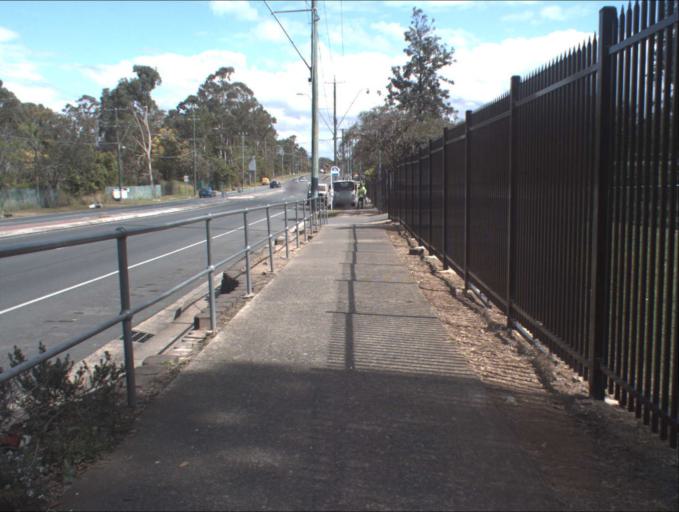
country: AU
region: Queensland
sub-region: Logan
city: Waterford West
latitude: -27.6867
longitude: 153.1065
